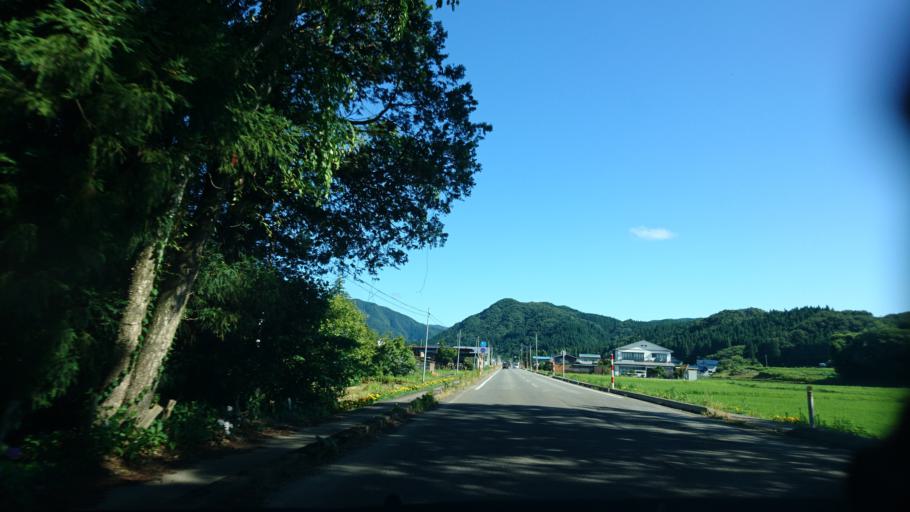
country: JP
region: Akita
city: Kakunodatemachi
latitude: 39.6684
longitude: 140.5680
